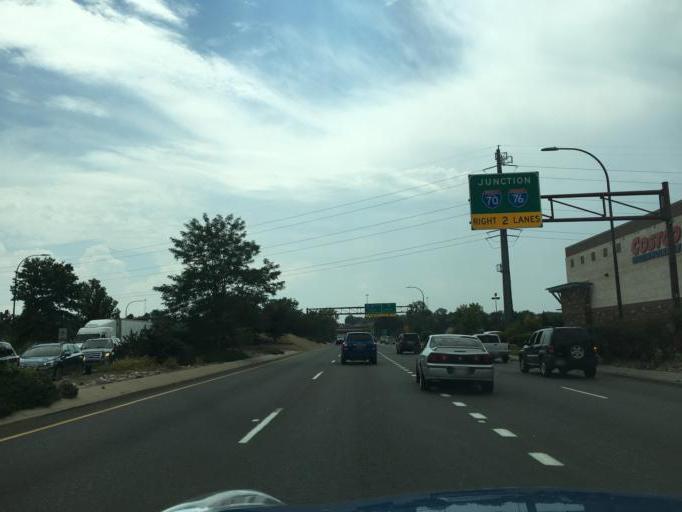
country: US
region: Colorado
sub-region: Jefferson County
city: Arvada
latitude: 39.7902
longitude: -105.0815
